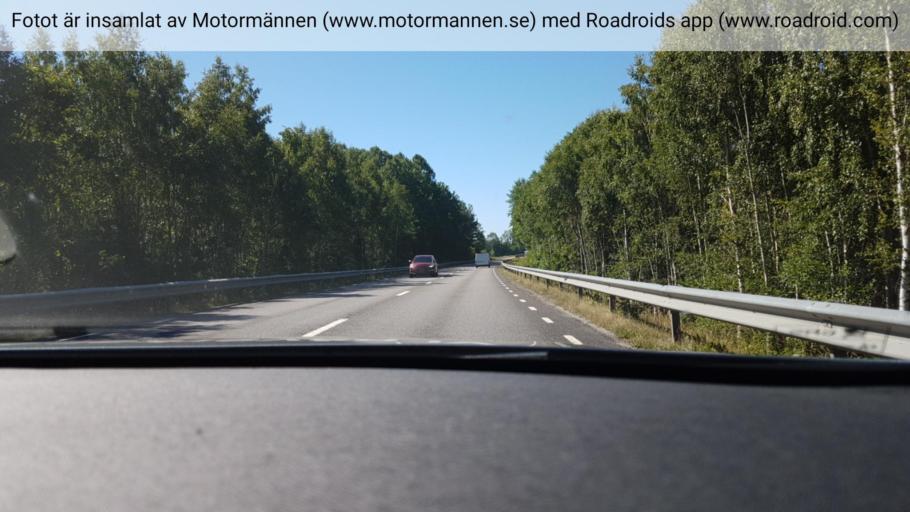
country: SE
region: Joenkoeping
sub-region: Habo Kommun
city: Habo
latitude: 57.9579
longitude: 14.1066
